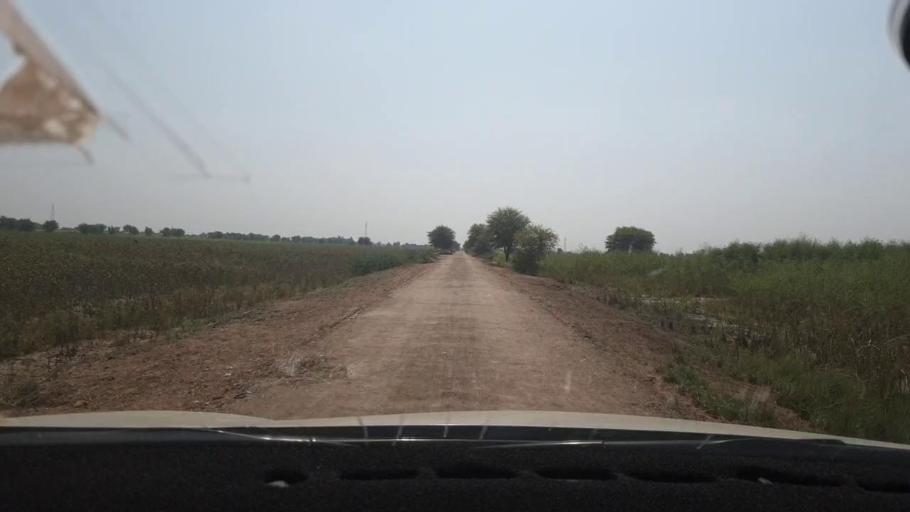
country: PK
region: Sindh
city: Tando Mittha Khan
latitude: 25.9105
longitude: 69.2066
